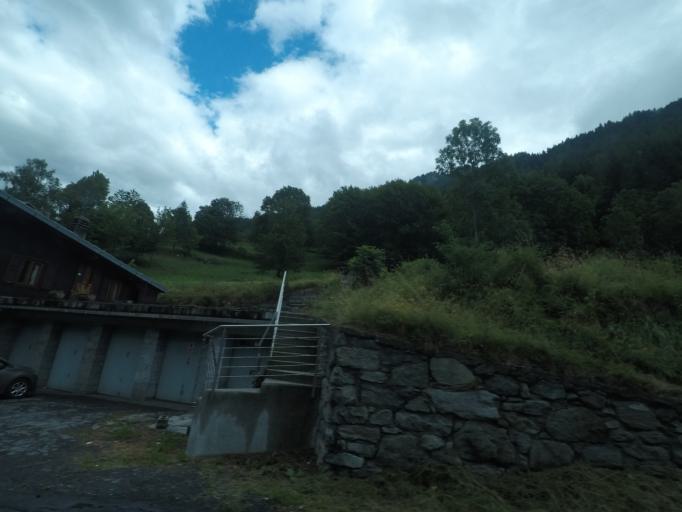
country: IT
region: Aosta Valley
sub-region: Valle d'Aosta
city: Valtournenche
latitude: 45.8662
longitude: 7.6170
